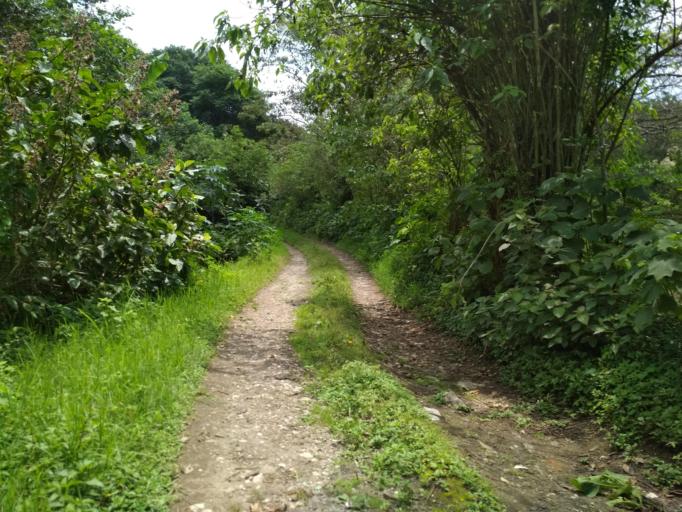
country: MX
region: Veracruz
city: Jilotepec
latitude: 19.6184
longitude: -96.9316
